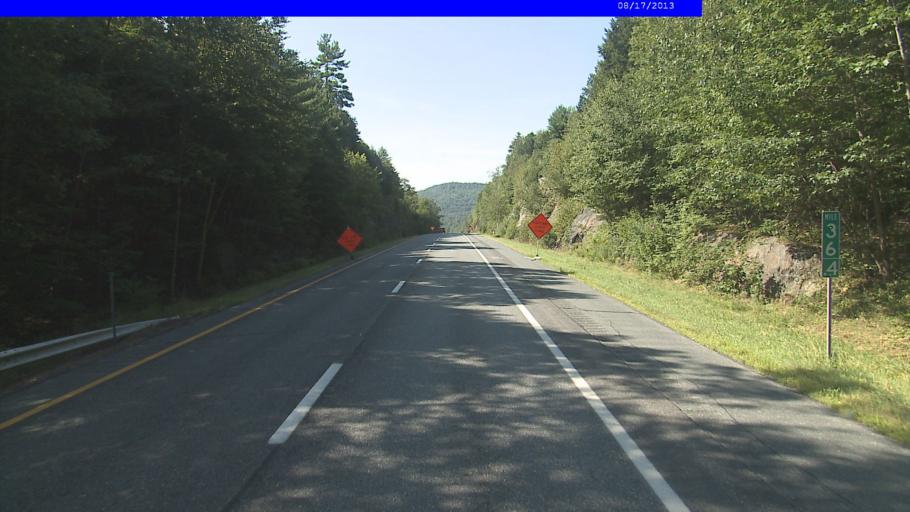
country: US
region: Vermont
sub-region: Windham County
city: Rockingham
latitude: 43.1950
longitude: -72.4575
